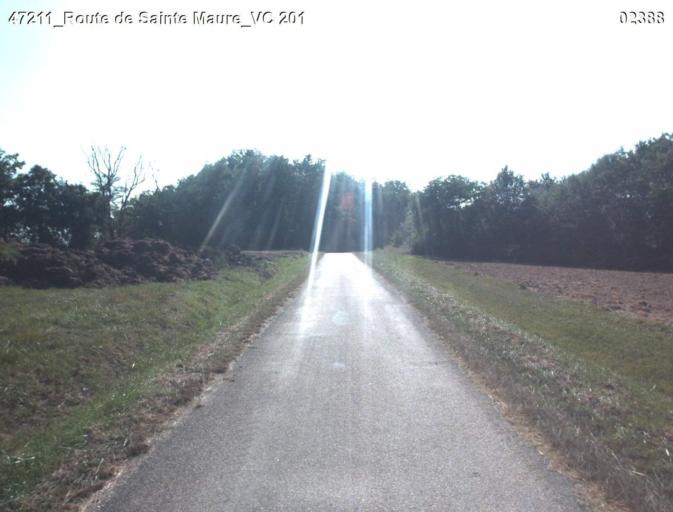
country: FR
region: Midi-Pyrenees
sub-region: Departement du Gers
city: Montreal
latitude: 44.0256
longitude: 0.1806
